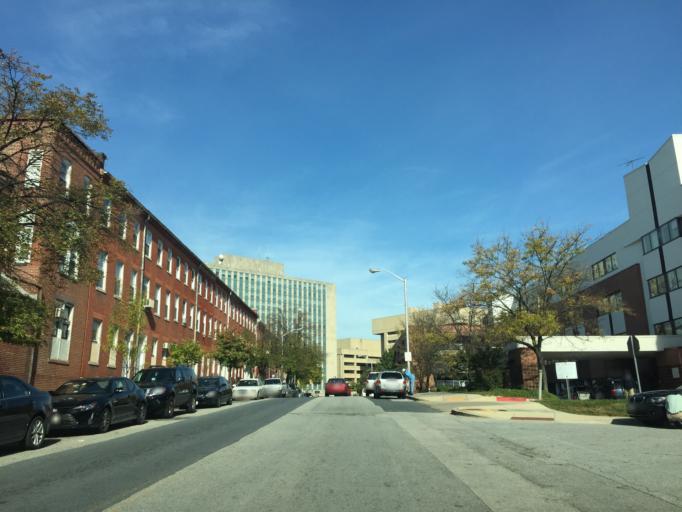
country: US
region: Maryland
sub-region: City of Baltimore
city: Baltimore
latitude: 39.2991
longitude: -76.6215
